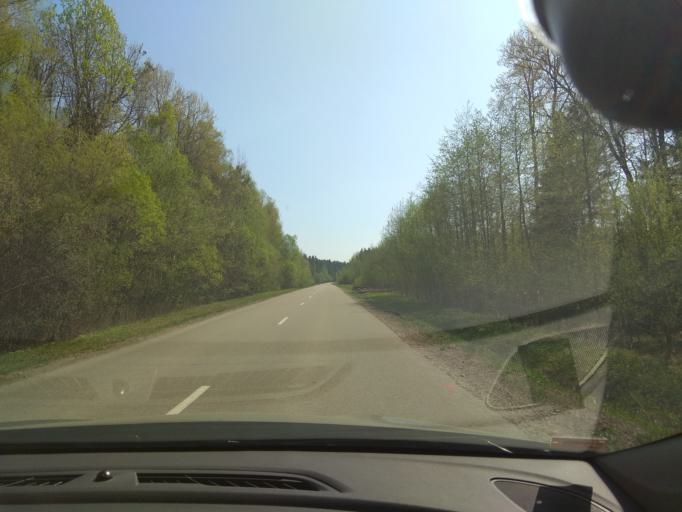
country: LT
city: Linkuva
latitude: 55.9928
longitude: 24.1732
